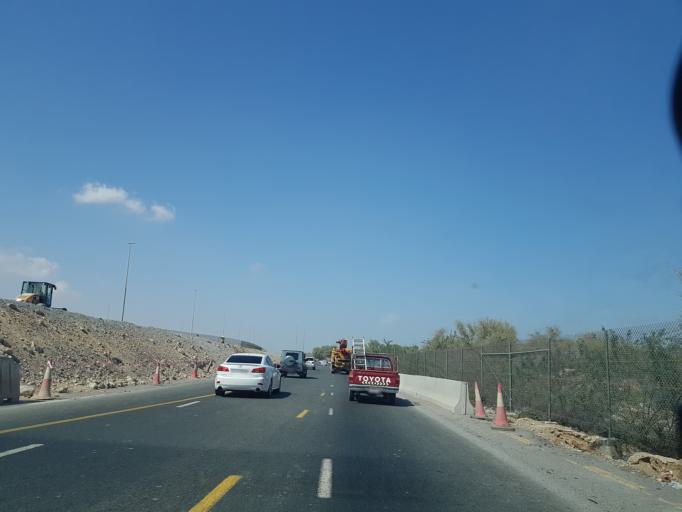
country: AE
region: Ra's al Khaymah
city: Ras al-Khaimah
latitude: 25.7023
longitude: 55.9701
